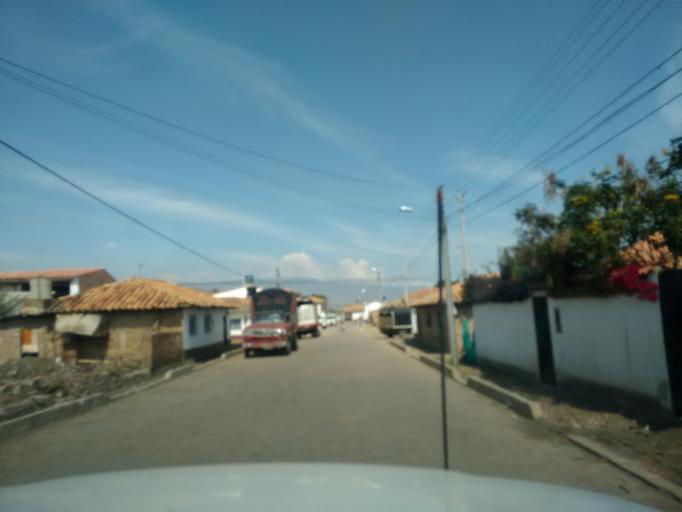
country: CO
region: Boyaca
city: Sachica
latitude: 5.5830
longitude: -73.5407
